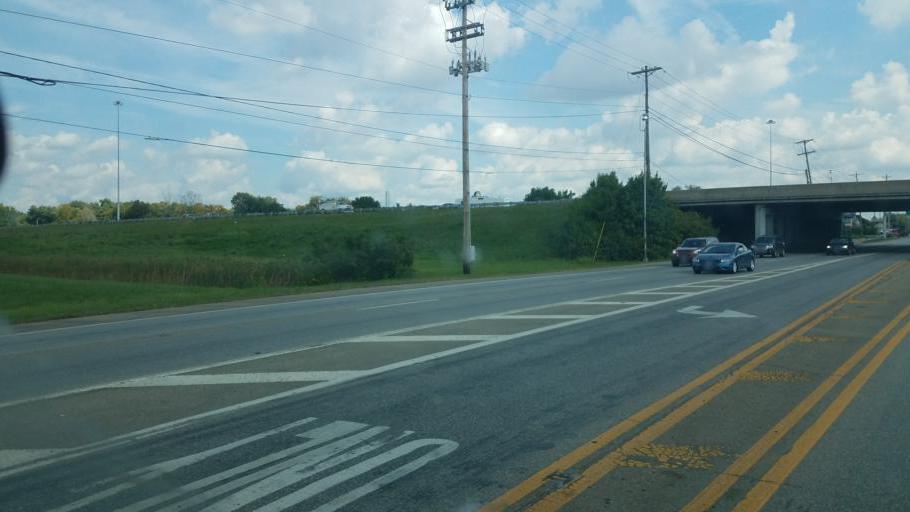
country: US
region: Ohio
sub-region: Franklin County
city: Worthington
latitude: 40.0876
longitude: -82.9884
